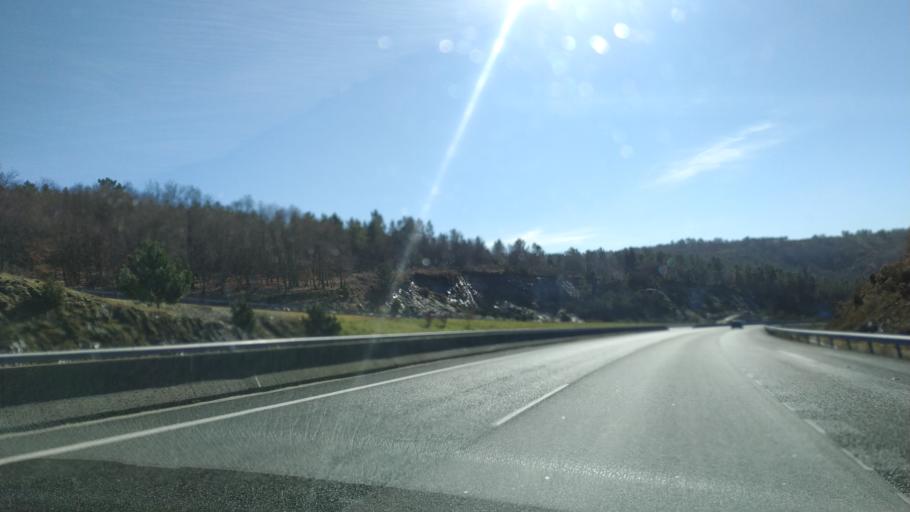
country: ES
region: Galicia
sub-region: Provincia de Pontevedra
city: Lalin
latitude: 42.6203
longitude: -8.0988
